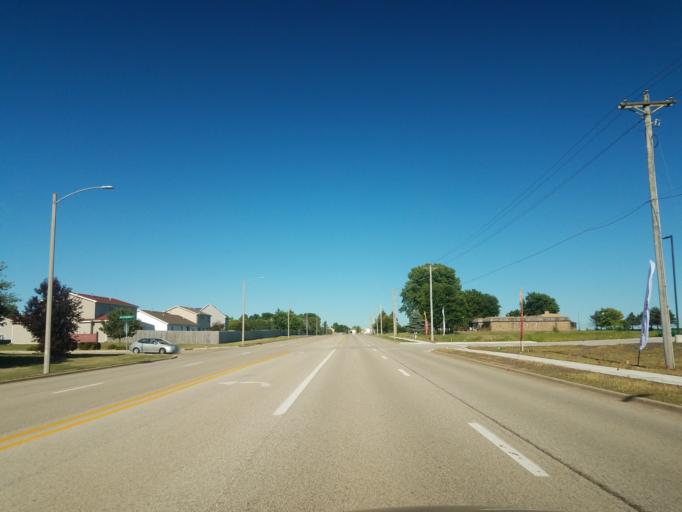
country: US
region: Illinois
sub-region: McLean County
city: Bloomington
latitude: 40.4590
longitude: -88.9307
